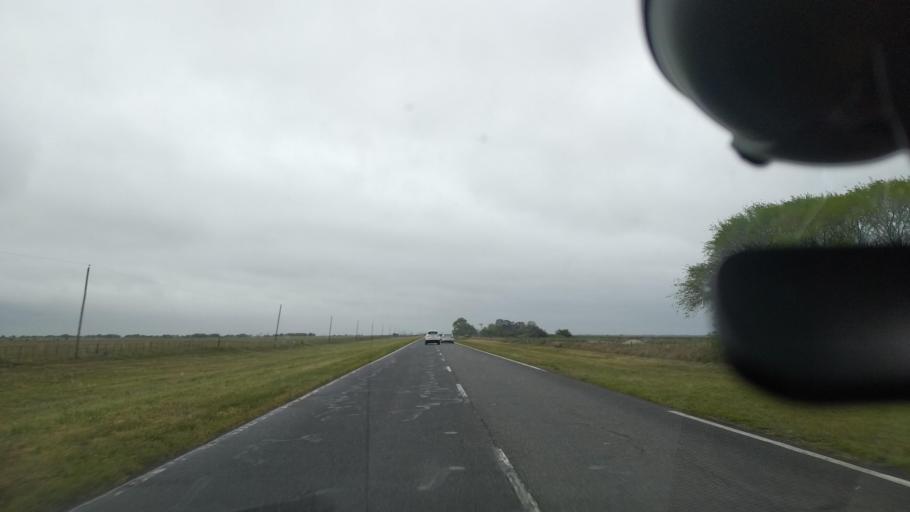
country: AR
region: Buenos Aires
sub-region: Partido de Dolores
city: Dolores
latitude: -36.1110
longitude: -57.4308
